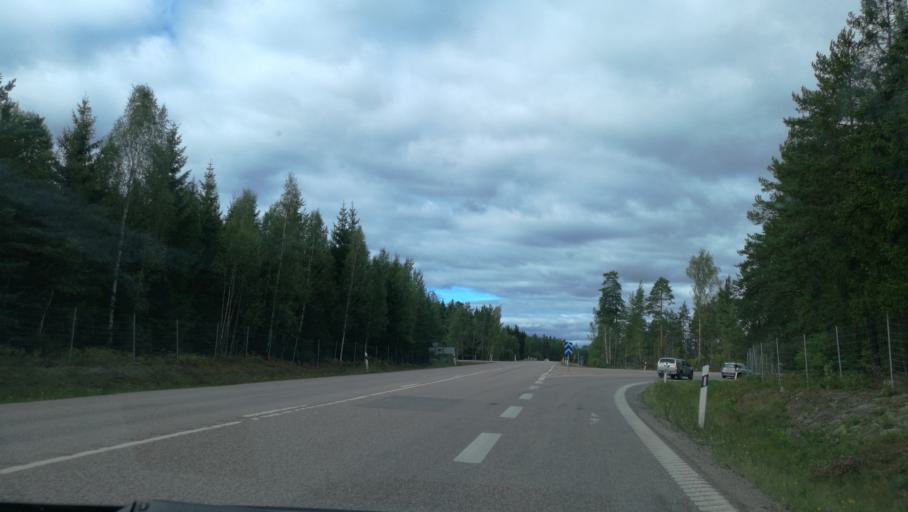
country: SE
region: Vaestmanland
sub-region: Hallstahammars Kommun
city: Kolback
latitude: 59.5782
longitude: 16.3529
